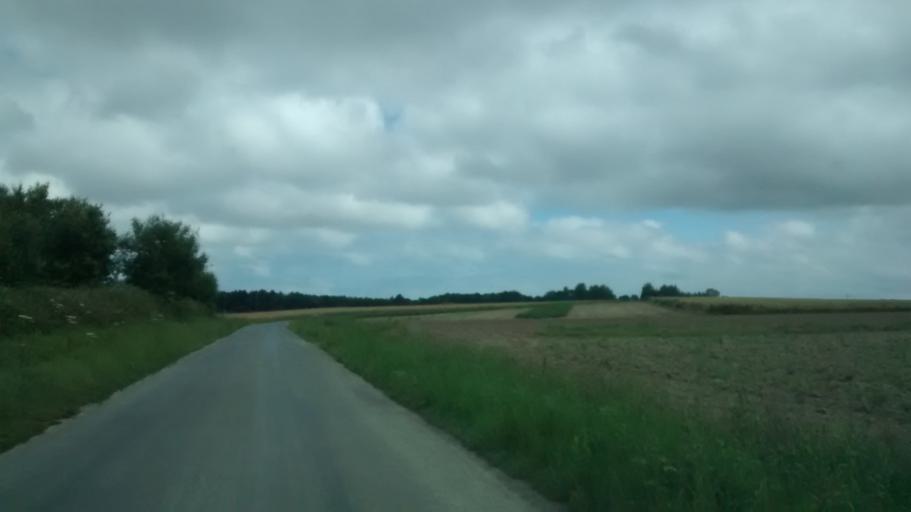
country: FR
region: Brittany
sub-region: Departement d'Ille-et-Vilaine
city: Saint-Meloir-des-Ondes
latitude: 48.6433
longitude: -1.9127
